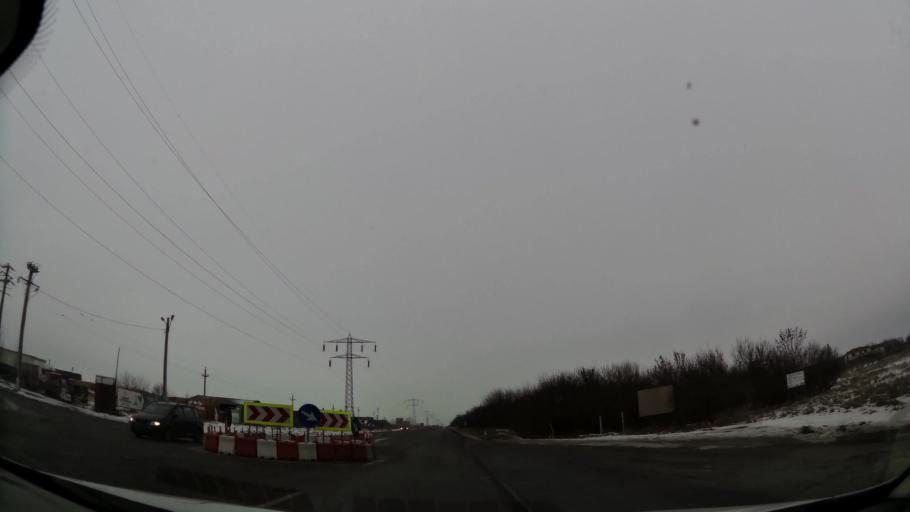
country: RO
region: Dambovita
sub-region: Comuna Tartasesti
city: Gulia
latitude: 44.5540
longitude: 25.8742
